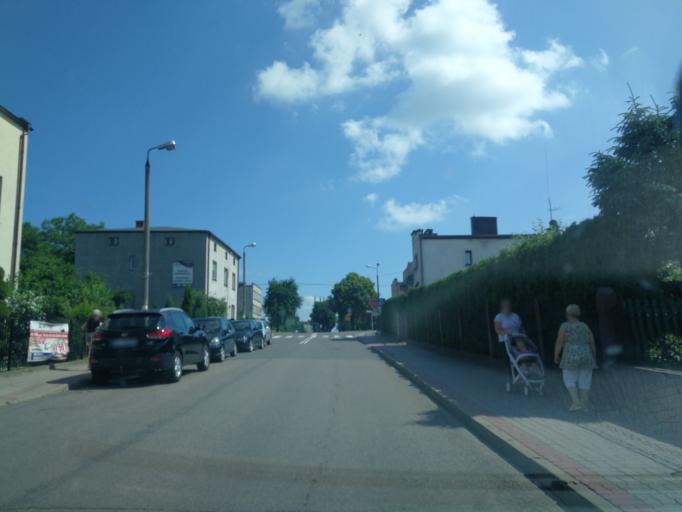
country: PL
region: Warmian-Masurian Voivodeship
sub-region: Powiat ilawski
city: Lubawa
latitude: 53.5021
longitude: 19.7502
